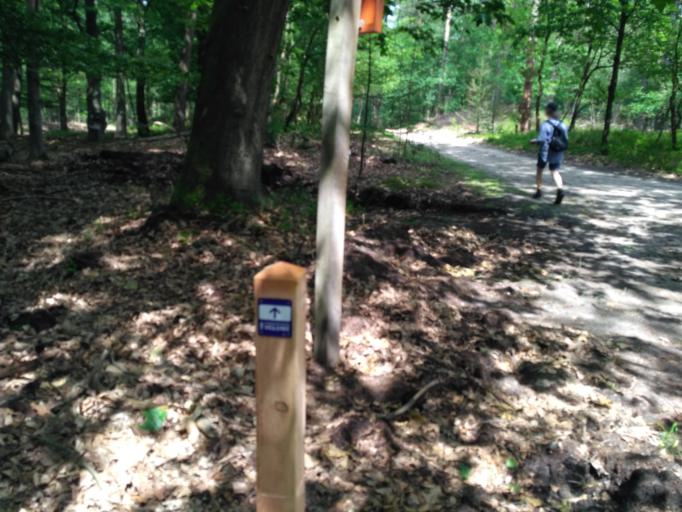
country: NL
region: Gelderland
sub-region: Gemeente Apeldoorn
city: Beekbergen
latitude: 52.1516
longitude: 5.9310
